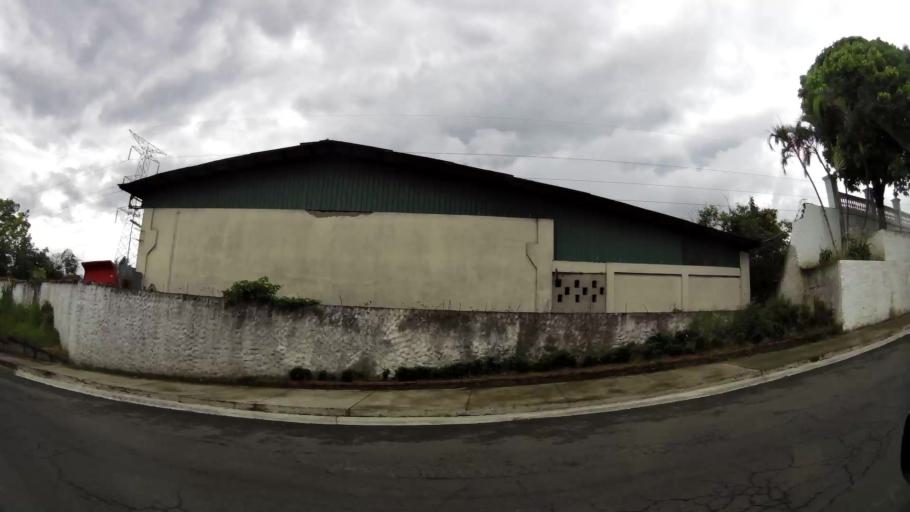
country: CR
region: San Jose
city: San Juan
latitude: 9.9704
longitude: -84.0880
